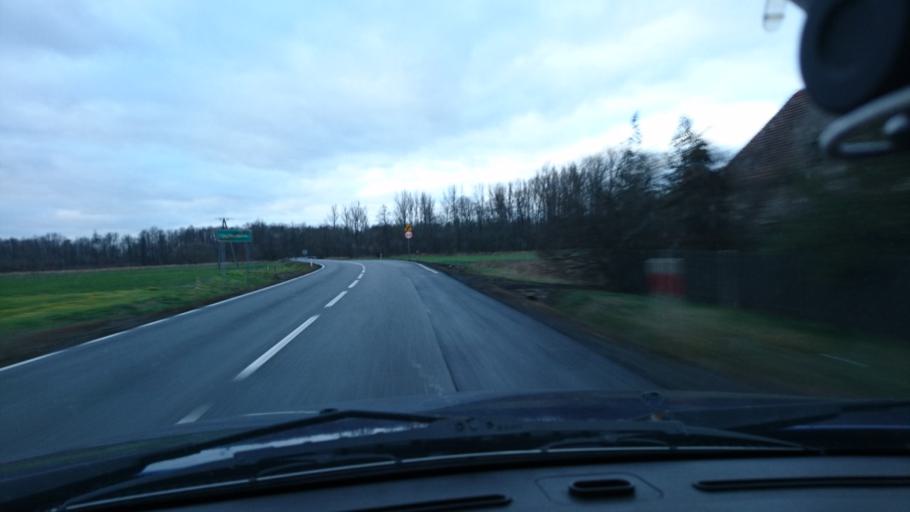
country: PL
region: Opole Voivodeship
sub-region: Powiat kluczborski
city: Byczyna
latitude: 51.1417
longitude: 18.1945
